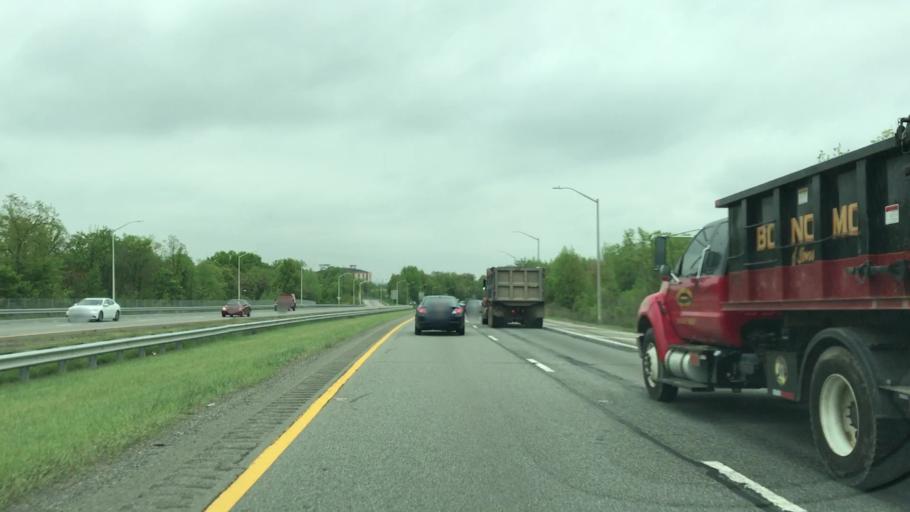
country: US
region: New Jersey
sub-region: Middlesex County
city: Carteret
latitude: 40.5422
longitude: -74.2237
